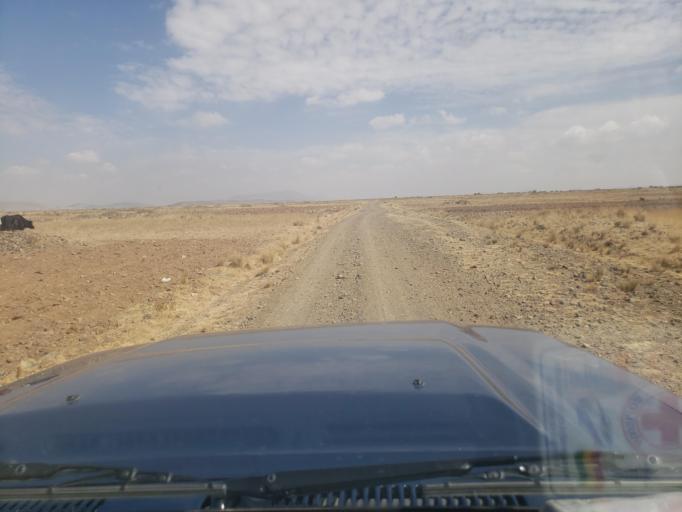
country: BO
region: La Paz
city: Batallas
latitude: -16.4229
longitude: -68.4072
